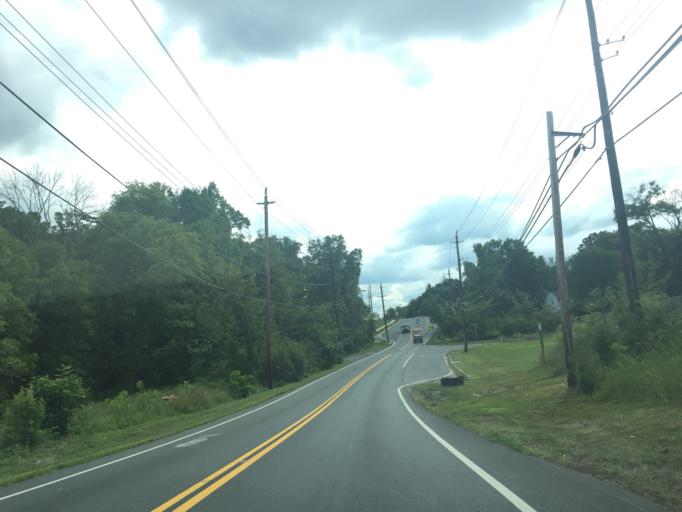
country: US
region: Maryland
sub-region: Montgomery County
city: Redland
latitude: 39.1555
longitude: -77.1556
